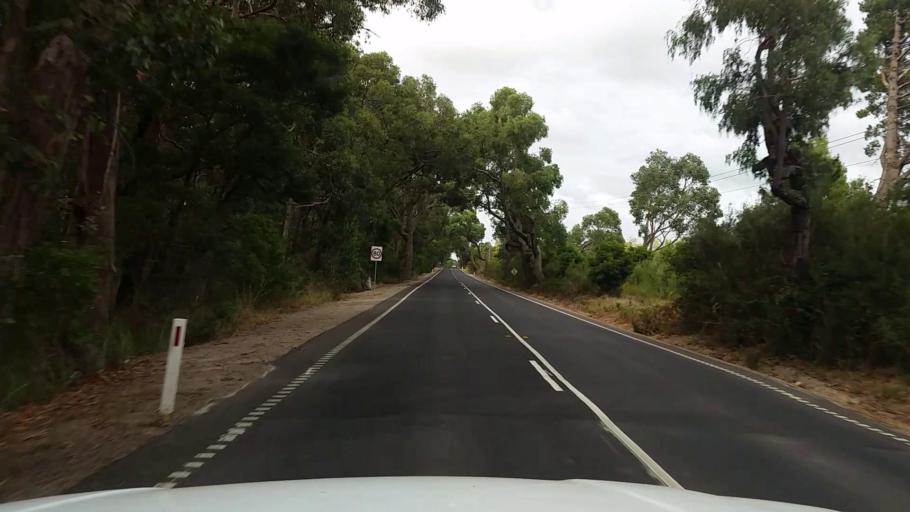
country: AU
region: Victoria
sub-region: Mornington Peninsula
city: Balnarring
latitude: -38.3398
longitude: 145.0978
